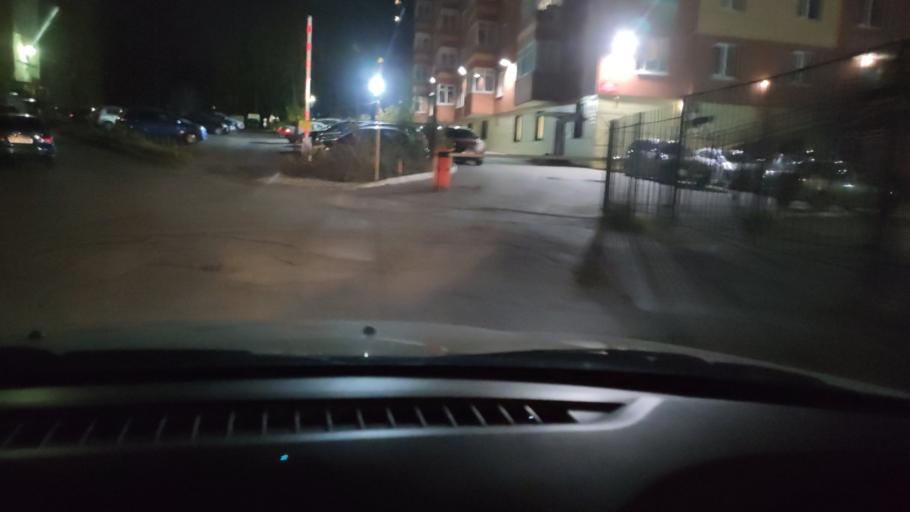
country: RU
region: Perm
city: Perm
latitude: 57.9894
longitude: 56.2334
